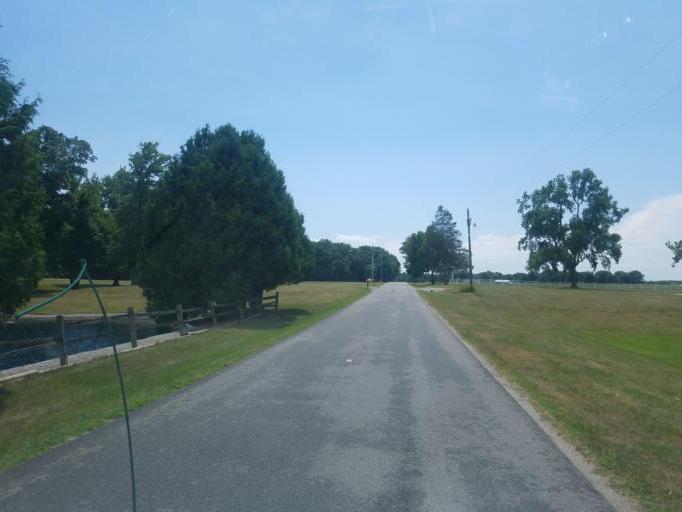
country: US
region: Ohio
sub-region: Paulding County
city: Antwerp
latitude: 41.1828
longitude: -84.7856
